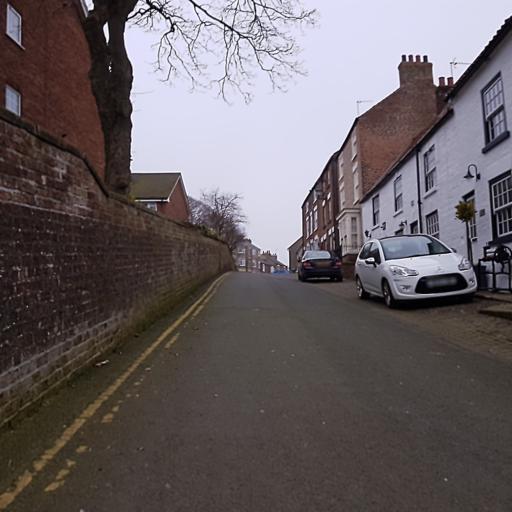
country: GB
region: England
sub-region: North Yorkshire
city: Filey
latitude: 54.2129
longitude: -0.2888
